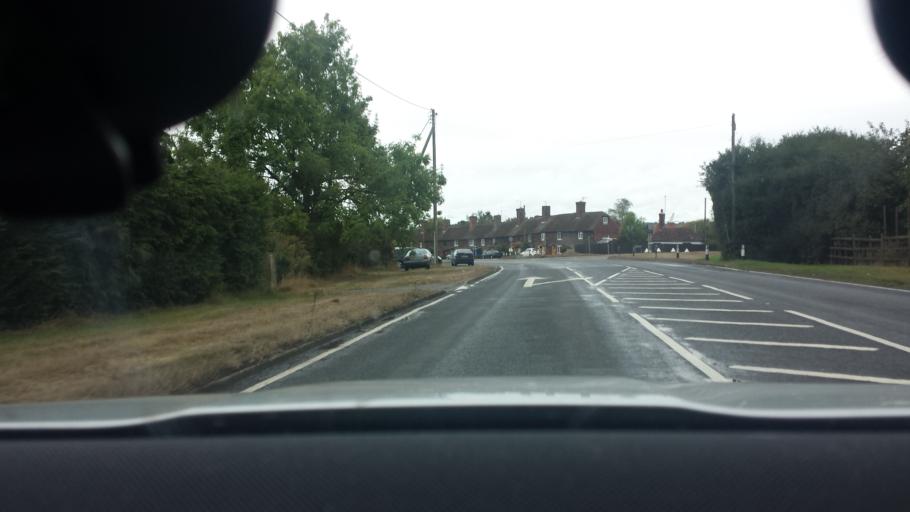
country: GB
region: England
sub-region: Kent
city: Staplehurst
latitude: 51.1870
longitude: 0.5474
